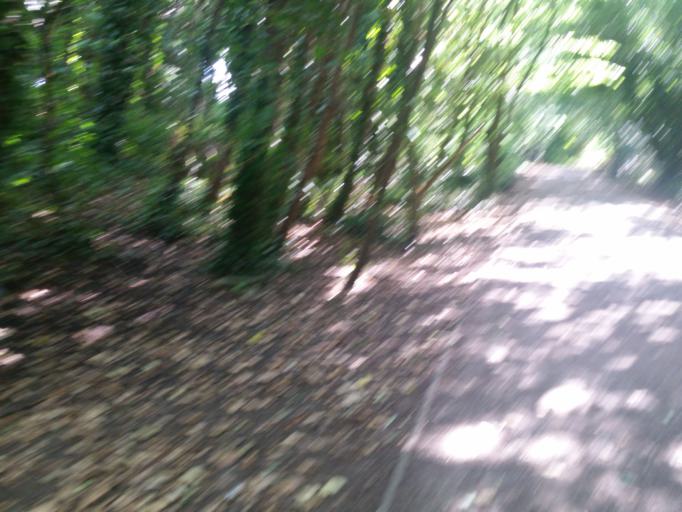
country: GB
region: England
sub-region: Greater London
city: Crouch End
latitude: 51.5876
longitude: -0.1431
